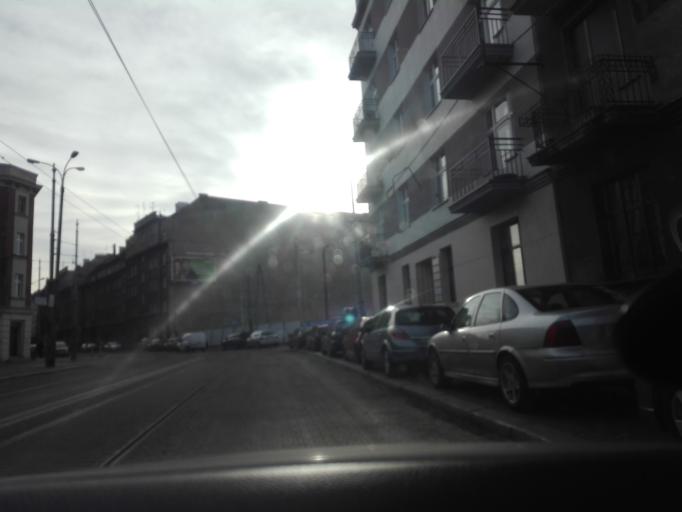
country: PL
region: Silesian Voivodeship
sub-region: Katowice
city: Katowice
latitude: 50.2619
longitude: 19.0088
